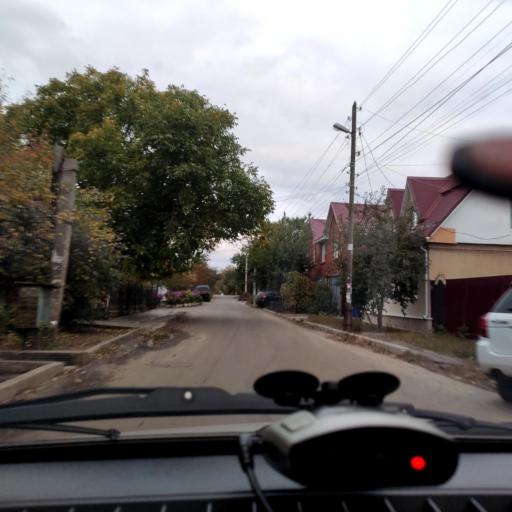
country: RU
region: Voronezj
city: Voronezh
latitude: 51.6336
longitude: 39.1678
